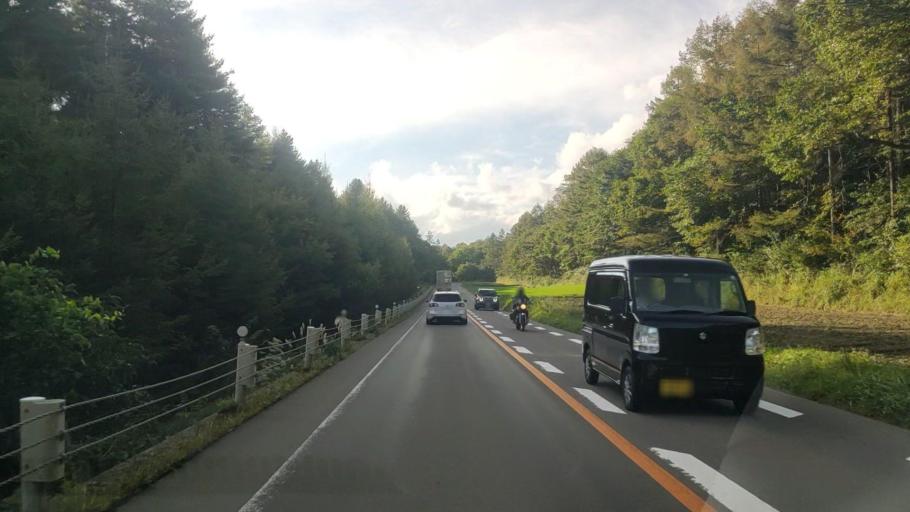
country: JP
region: Nagano
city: Ueda
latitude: 36.4860
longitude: 138.4260
